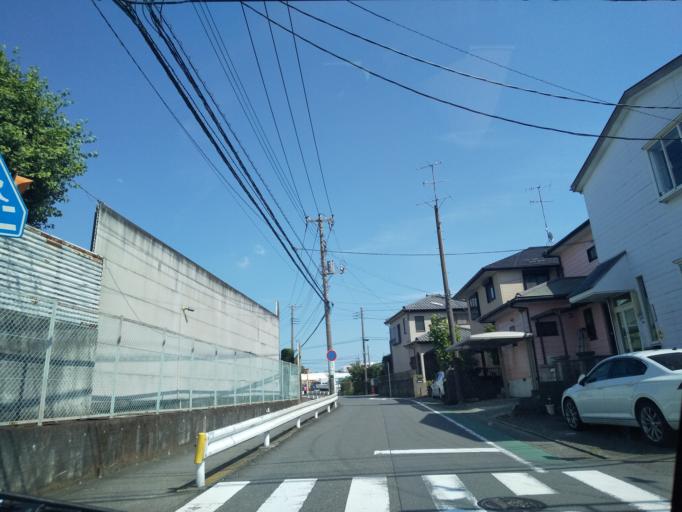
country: JP
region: Kanagawa
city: Zama
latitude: 35.4605
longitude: 139.4113
